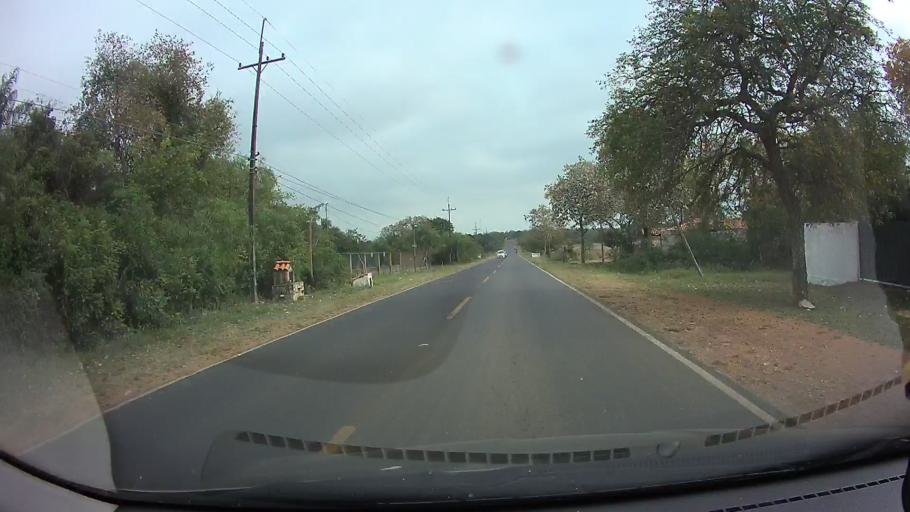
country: PY
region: Cordillera
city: Emboscada
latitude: -25.1498
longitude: -57.3317
